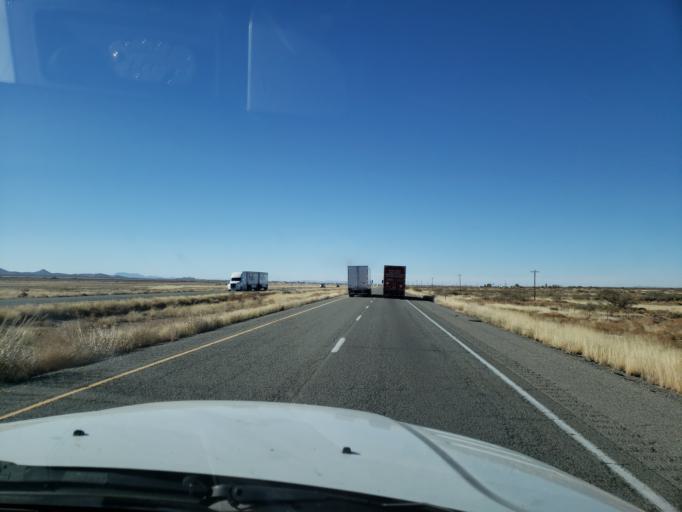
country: US
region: New Mexico
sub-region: Hidalgo County
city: Lordsburg
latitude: 32.3216
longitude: -108.6230
